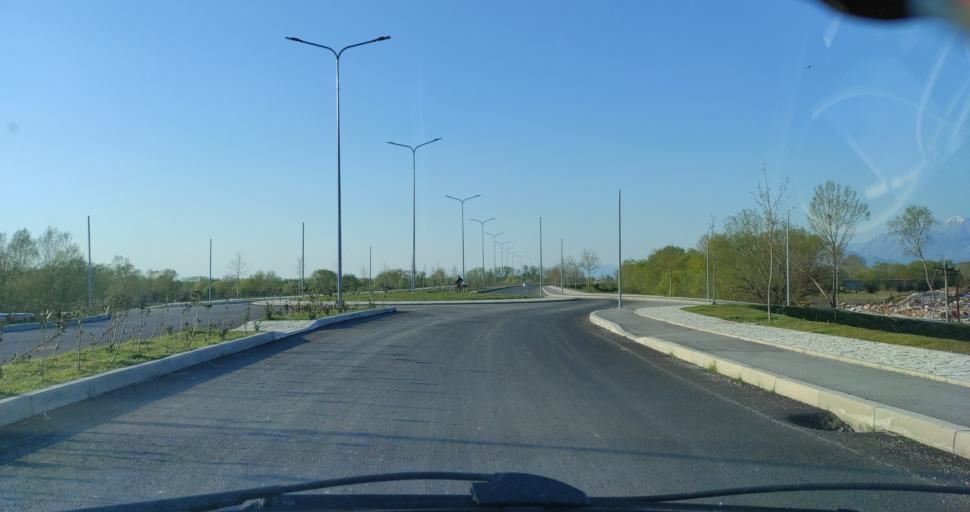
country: AL
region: Shkoder
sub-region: Rrethi i Shkodres
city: Shkoder
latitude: 42.0655
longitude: 19.4901
